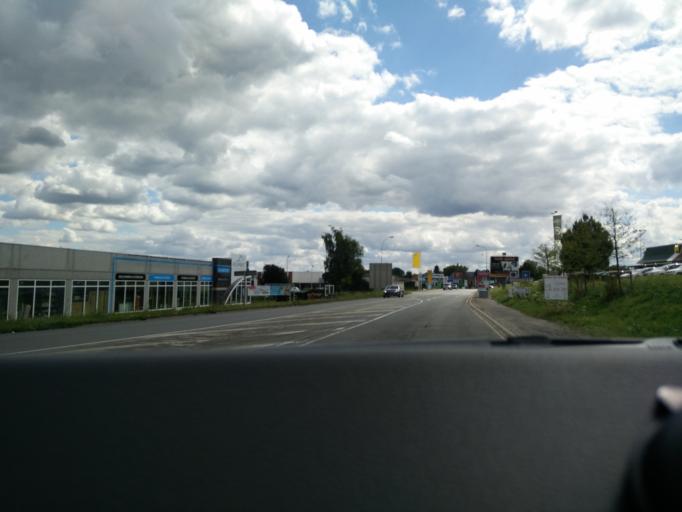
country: FR
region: Nord-Pas-de-Calais
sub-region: Departement du Nord
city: Hazebrouck
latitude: 50.7401
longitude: 2.5478
